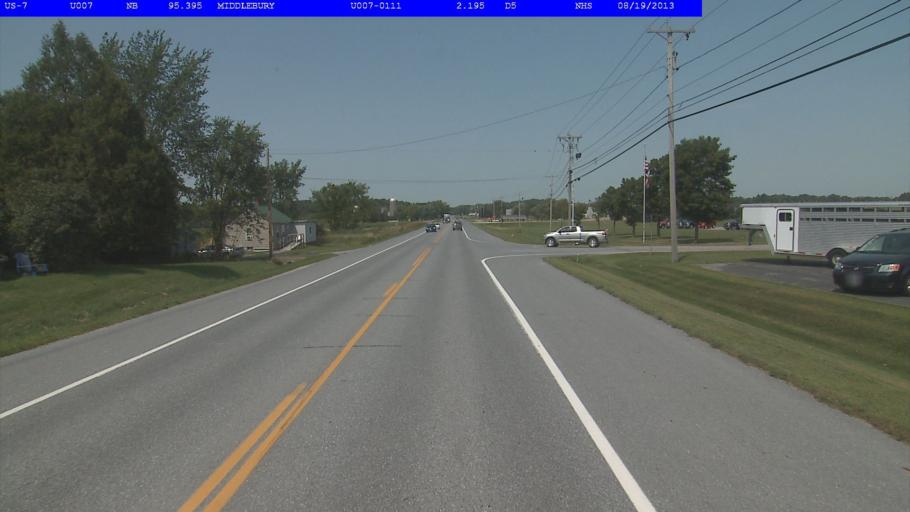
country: US
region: Vermont
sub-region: Addison County
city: Middlebury (village)
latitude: 43.9840
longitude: -73.1293
